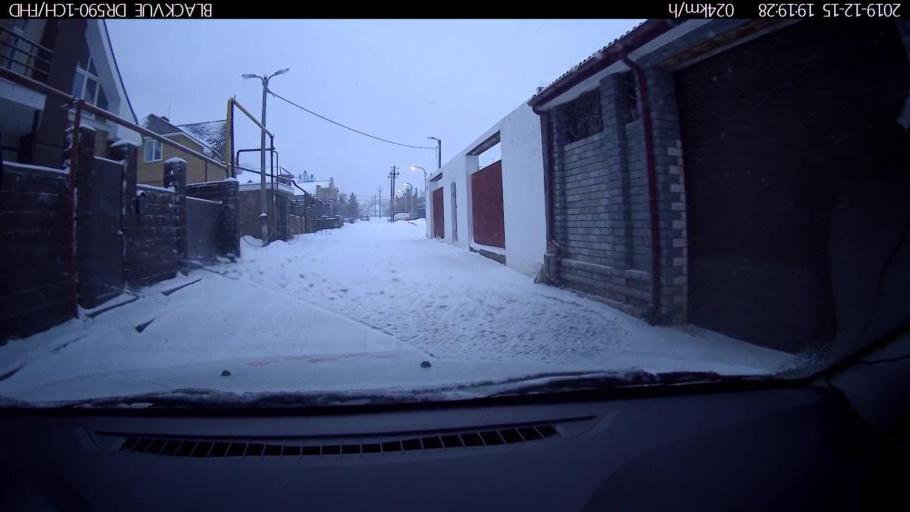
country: RU
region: Nizjnij Novgorod
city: Afonino
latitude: 56.3040
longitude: 44.0887
